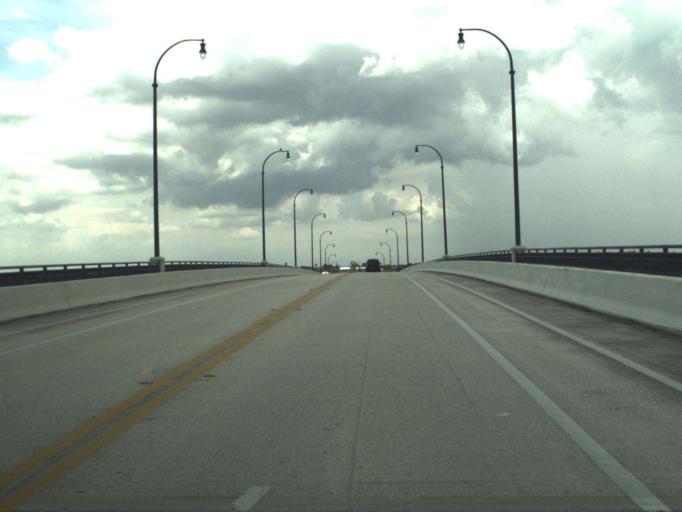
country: US
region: Florida
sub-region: Martin County
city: Jensen Beach
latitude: 27.2536
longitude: -80.2184
